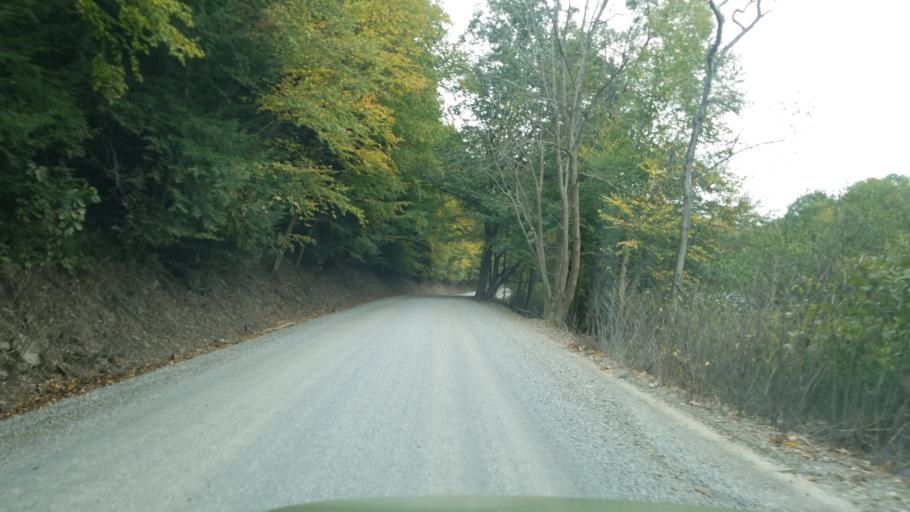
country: US
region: Pennsylvania
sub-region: Clearfield County
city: Curwensville
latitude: 40.9715
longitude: -78.4887
